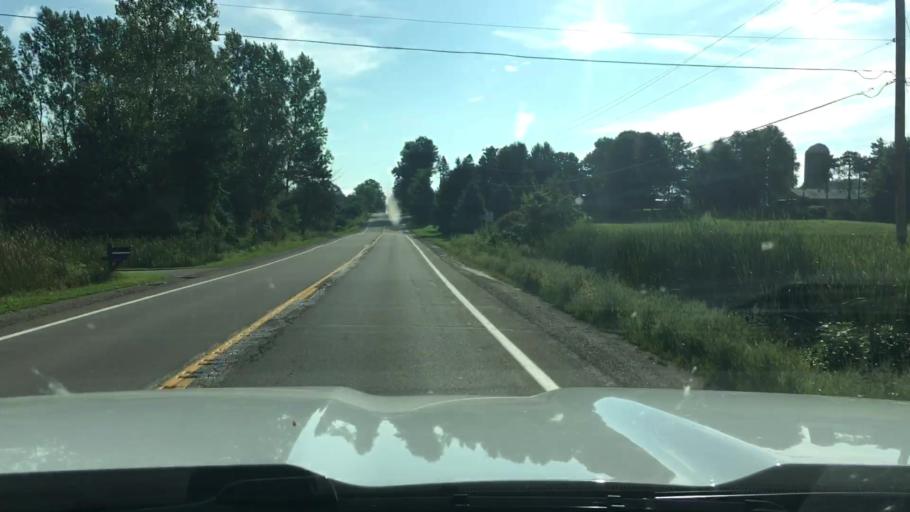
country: US
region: Michigan
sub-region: Kent County
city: Cedar Springs
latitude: 43.2194
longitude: -85.6304
